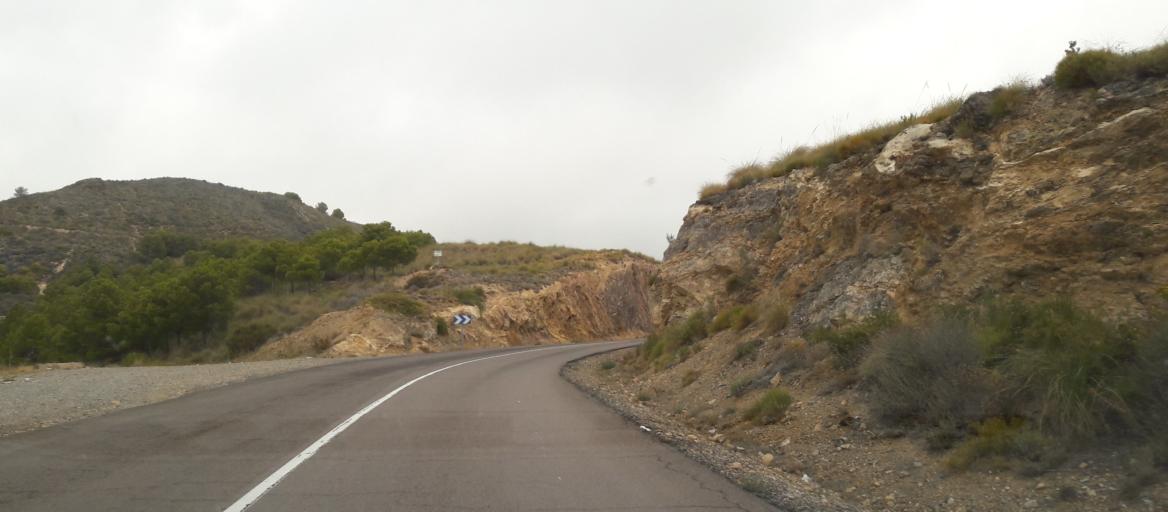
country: ES
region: Andalusia
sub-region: Provincia de Almeria
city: Enix
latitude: 36.8722
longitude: -2.6240
